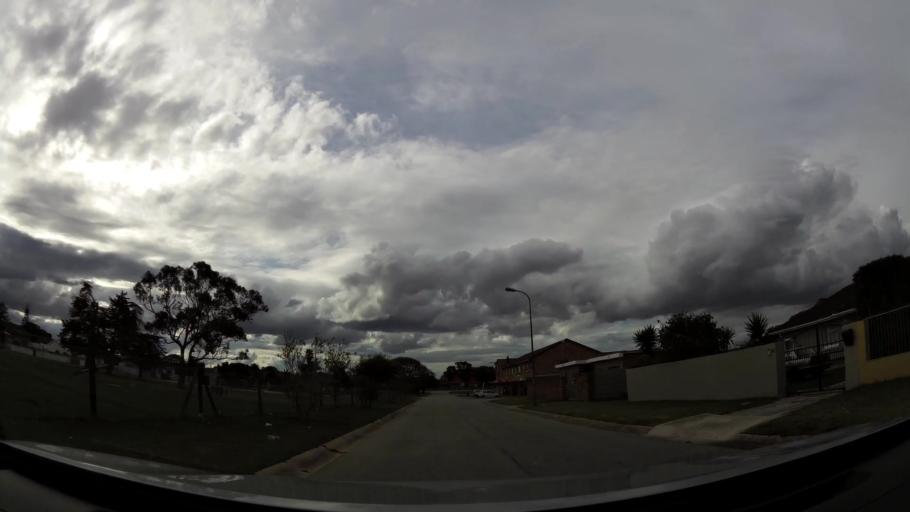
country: ZA
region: Eastern Cape
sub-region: Nelson Mandela Bay Metropolitan Municipality
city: Port Elizabeth
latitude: -33.9423
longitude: 25.4990
